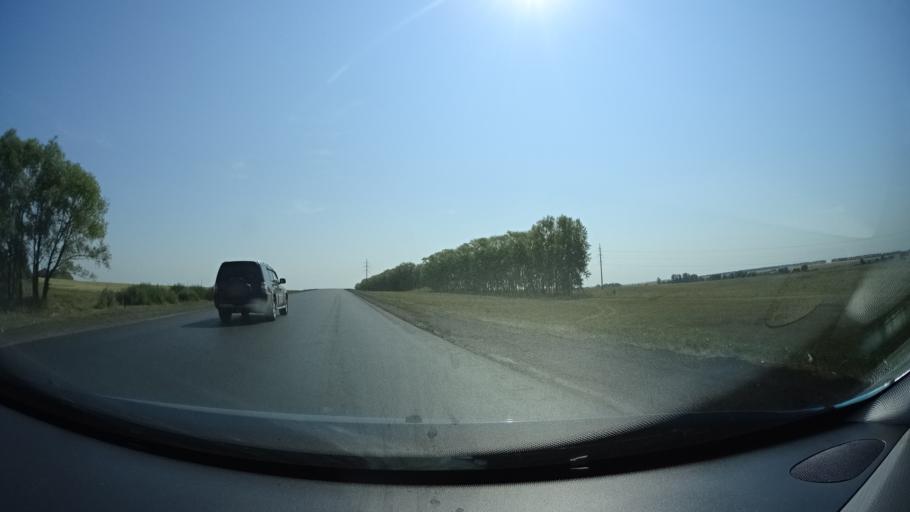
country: RU
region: Bashkortostan
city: Kabakovo
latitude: 54.4358
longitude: 56.0090
